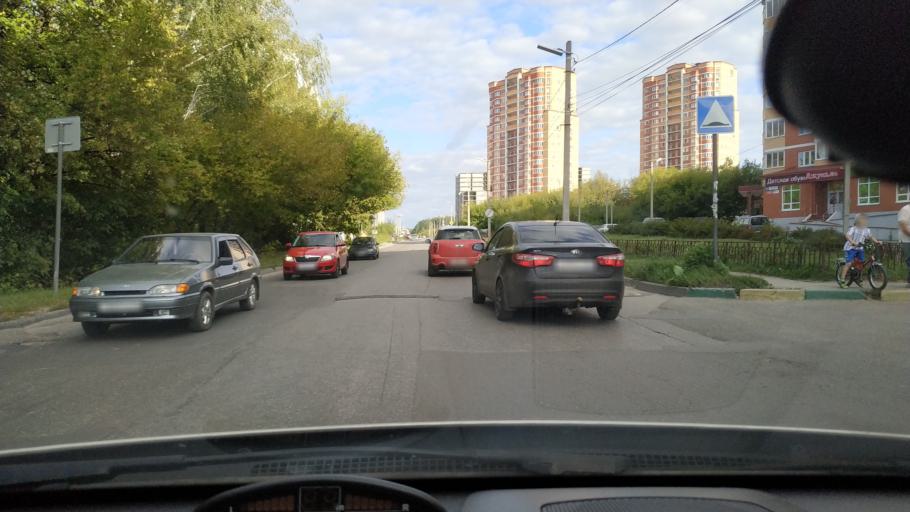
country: RU
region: Rjazan
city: Ryazan'
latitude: 54.6052
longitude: 39.7351
